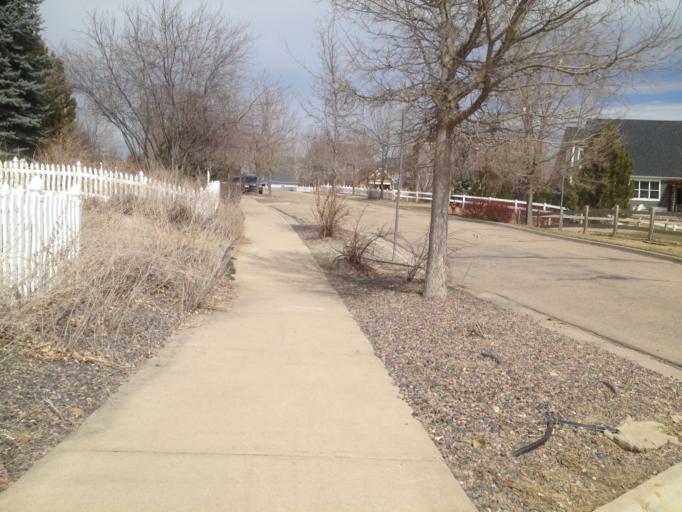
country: US
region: Colorado
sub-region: Boulder County
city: Louisville
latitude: 40.0052
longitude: -105.1399
